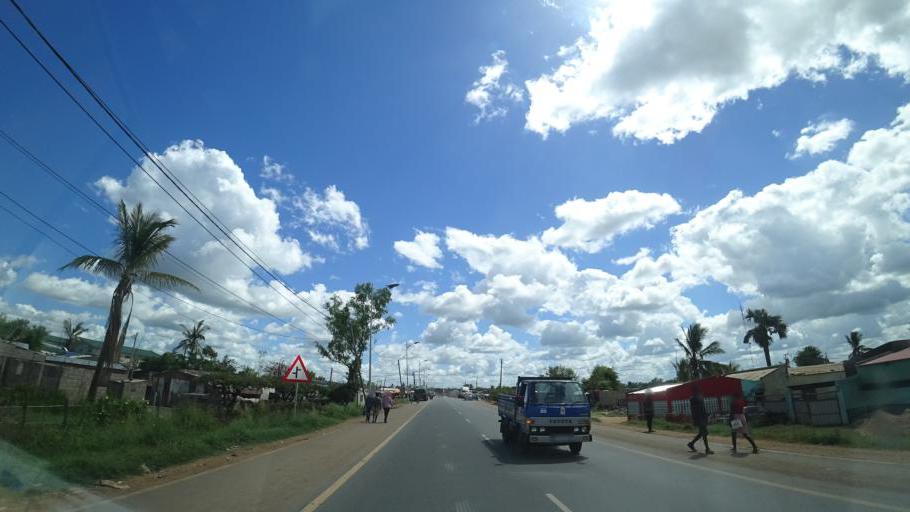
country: MZ
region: Sofala
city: Dondo
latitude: -19.2709
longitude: 34.2100
